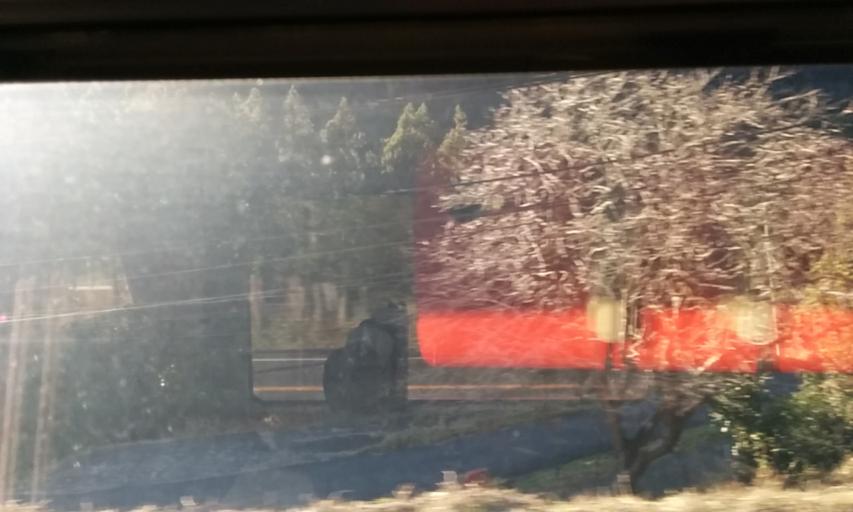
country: JP
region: Gifu
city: Nakatsugawa
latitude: 35.6472
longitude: 137.6178
